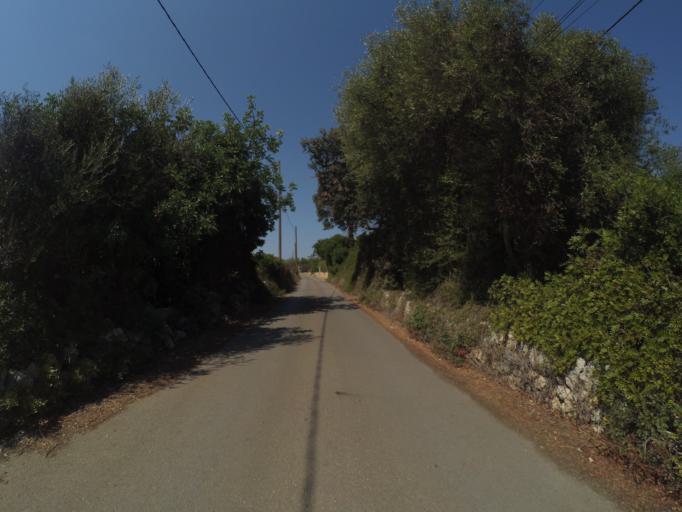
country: ES
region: Balearic Islands
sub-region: Illes Balears
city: Santanyi
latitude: 39.3894
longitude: 3.2402
